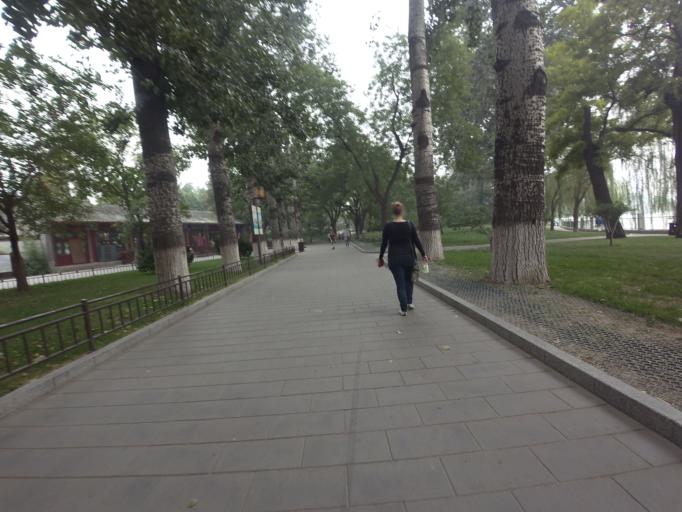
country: CN
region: Beijing
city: Jingshan
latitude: 39.9301
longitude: 116.3854
